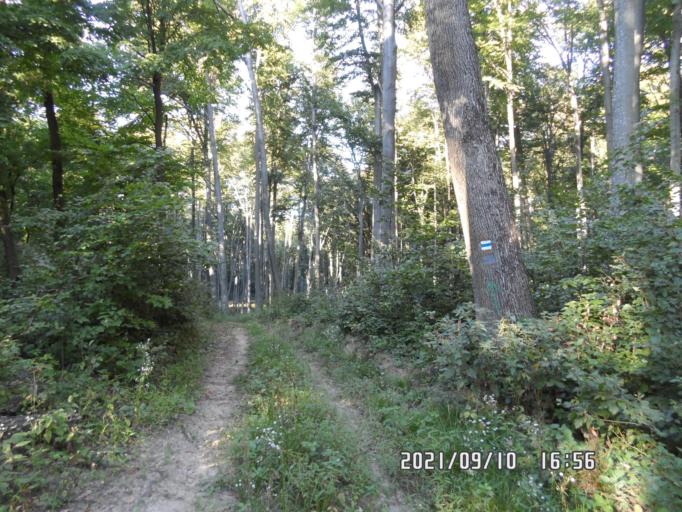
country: HU
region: Zala
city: Nagykanizsa
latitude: 46.5783
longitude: 17.0467
